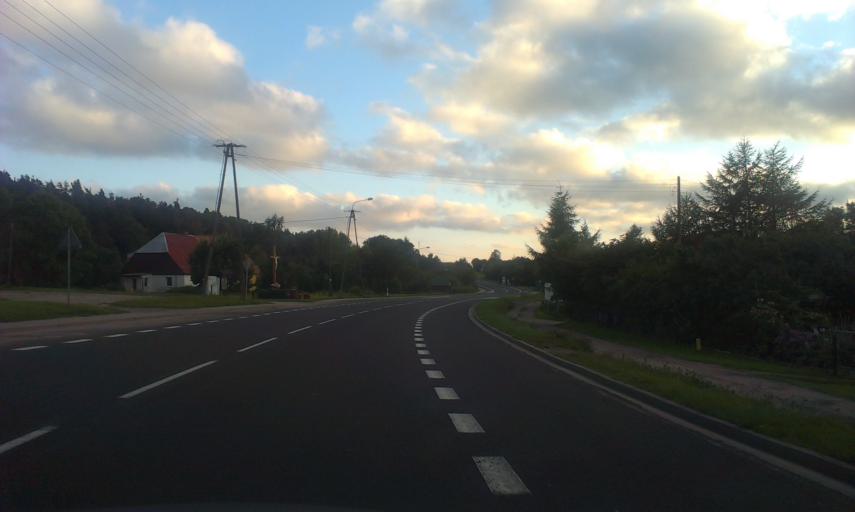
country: PL
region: West Pomeranian Voivodeship
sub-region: Powiat koszalinski
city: Sianow
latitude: 54.2711
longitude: 16.4259
